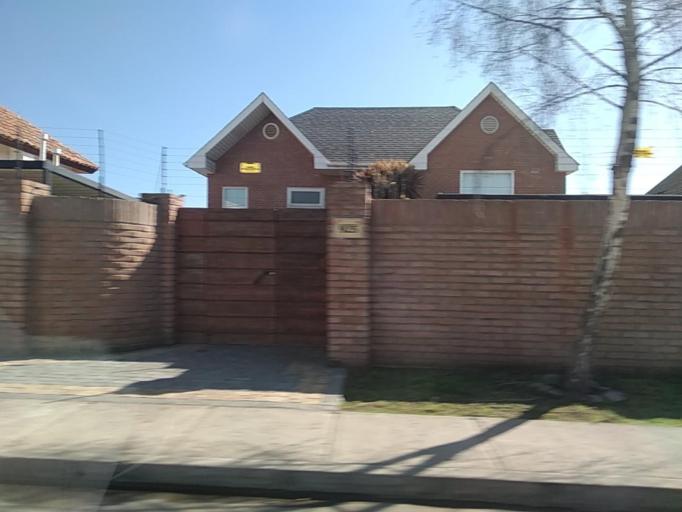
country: CL
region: Valparaiso
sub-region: Provincia de Valparaiso
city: Vina del Mar
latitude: -32.9412
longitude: -71.5443
